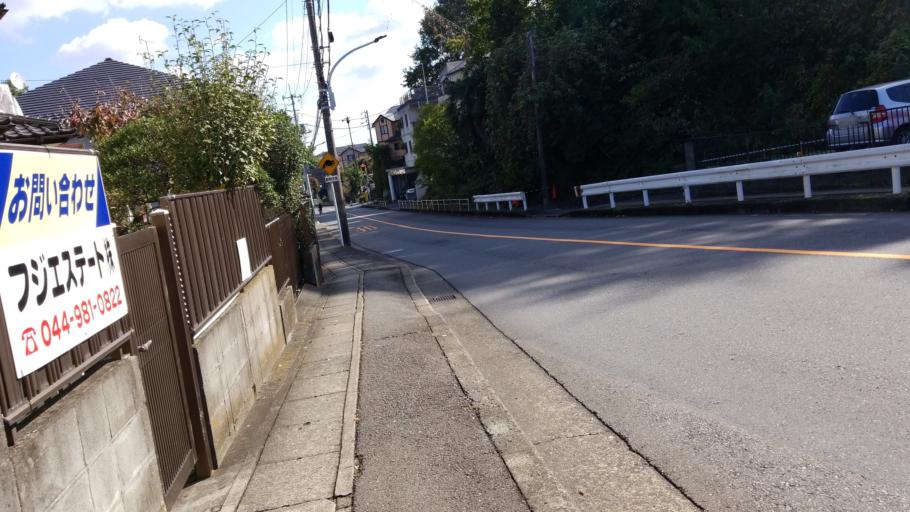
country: JP
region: Tokyo
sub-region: Machida-shi
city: Machida
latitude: 35.5857
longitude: 139.5036
